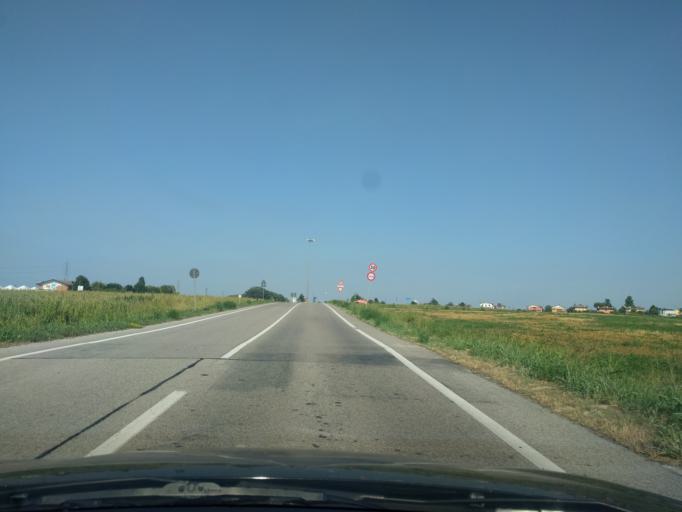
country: IT
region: Veneto
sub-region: Provincia di Rovigo
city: Mardimago
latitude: 45.0914
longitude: 11.8252
